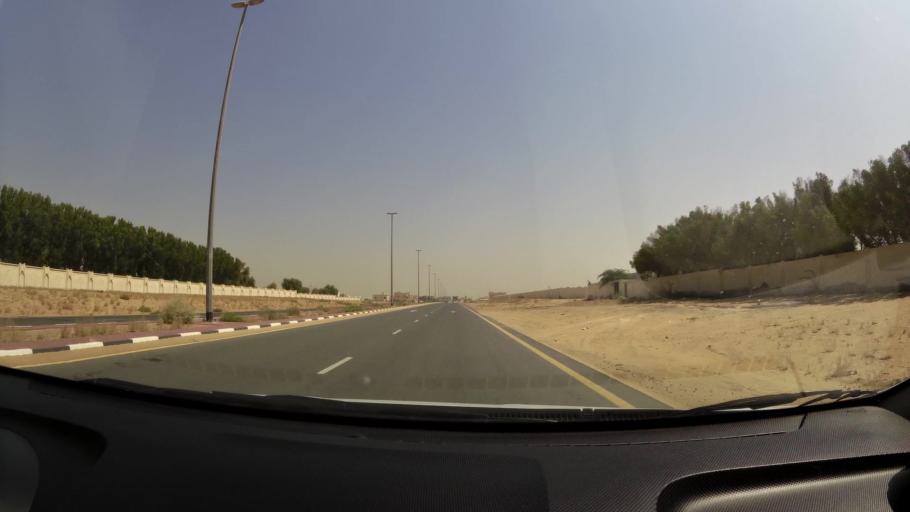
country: AE
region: Ajman
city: Ajman
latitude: 25.3987
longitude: 55.5373
